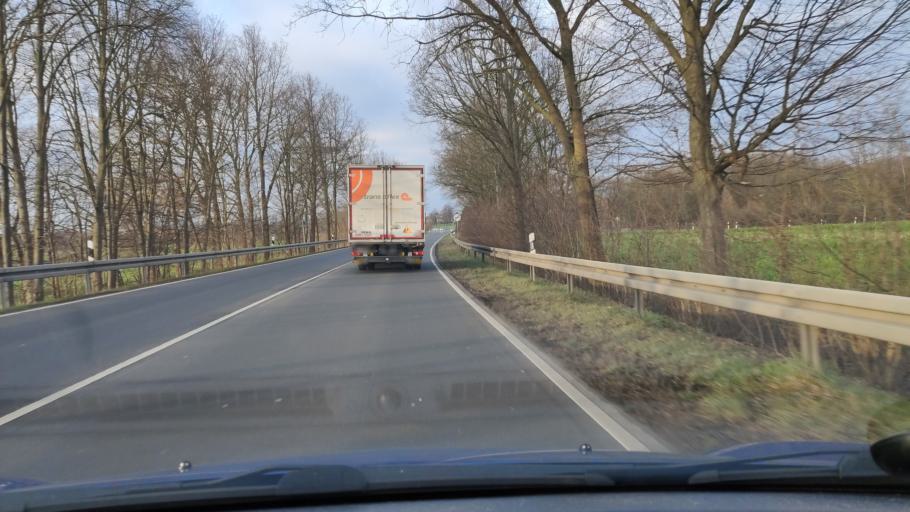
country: DE
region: Lower Saxony
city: Messenkamp
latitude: 52.2611
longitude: 9.3743
